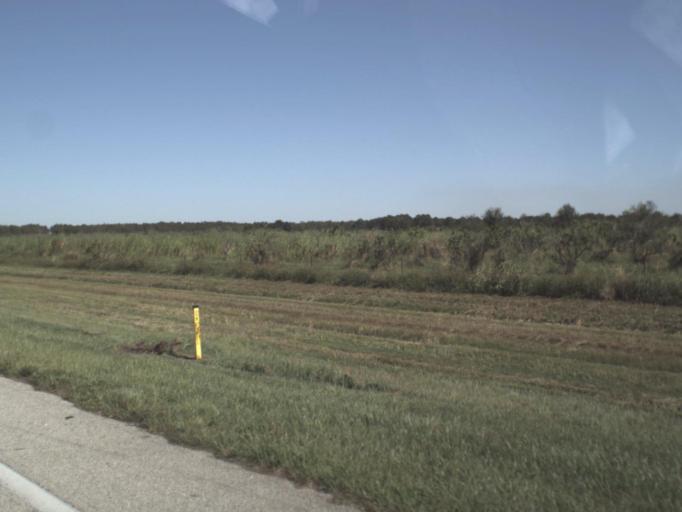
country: US
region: Florida
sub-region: Hendry County
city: LaBelle
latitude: 26.7353
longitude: -81.4739
